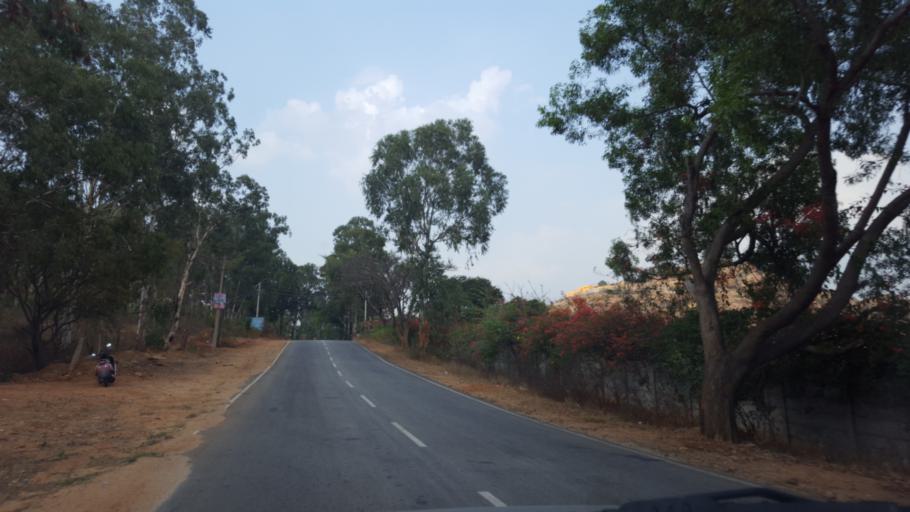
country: IN
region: Karnataka
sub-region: Chikkaballapur
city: Chik Ballapur
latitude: 13.3706
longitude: 77.6976
